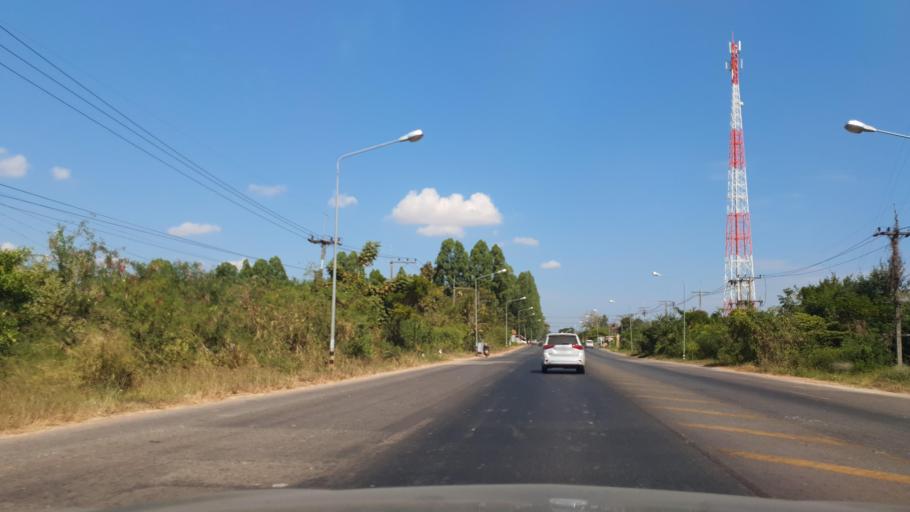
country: TH
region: Kalasin
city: Somdet
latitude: 16.7227
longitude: 103.7592
